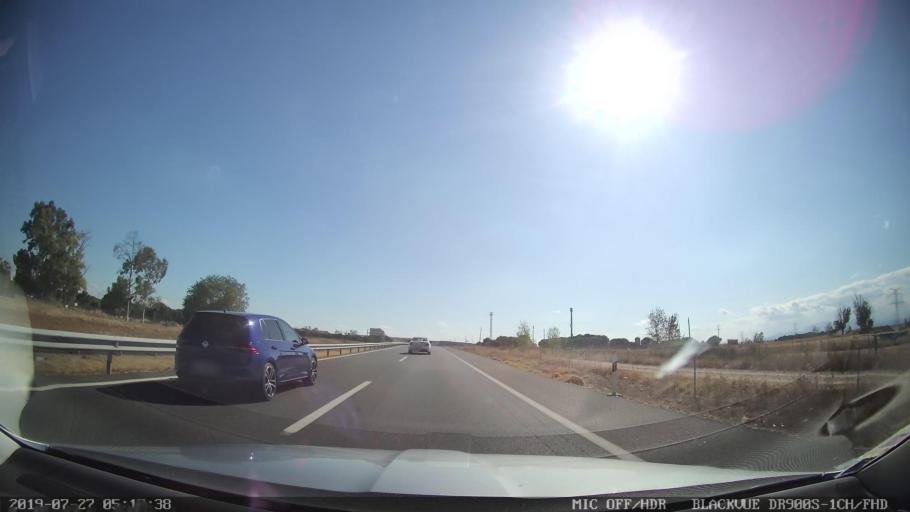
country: ES
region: Castille-La Mancha
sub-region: Province of Toledo
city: Maqueda
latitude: 40.0449
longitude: -4.3954
